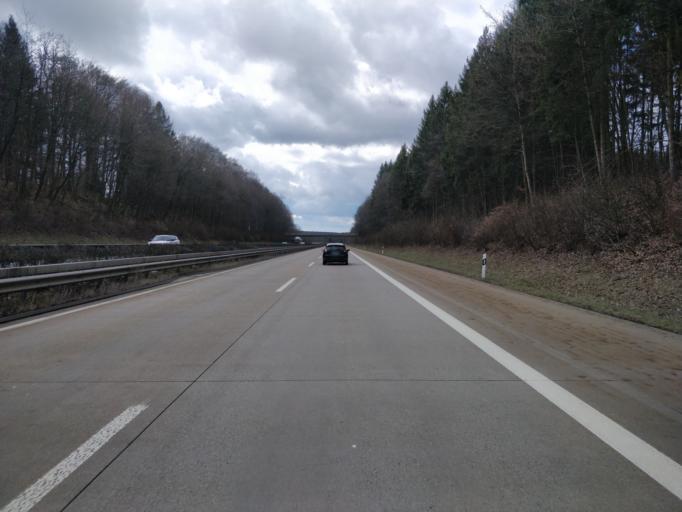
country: DE
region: Rheinland-Pfalz
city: Eckfeld
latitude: 50.1230
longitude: 6.8547
